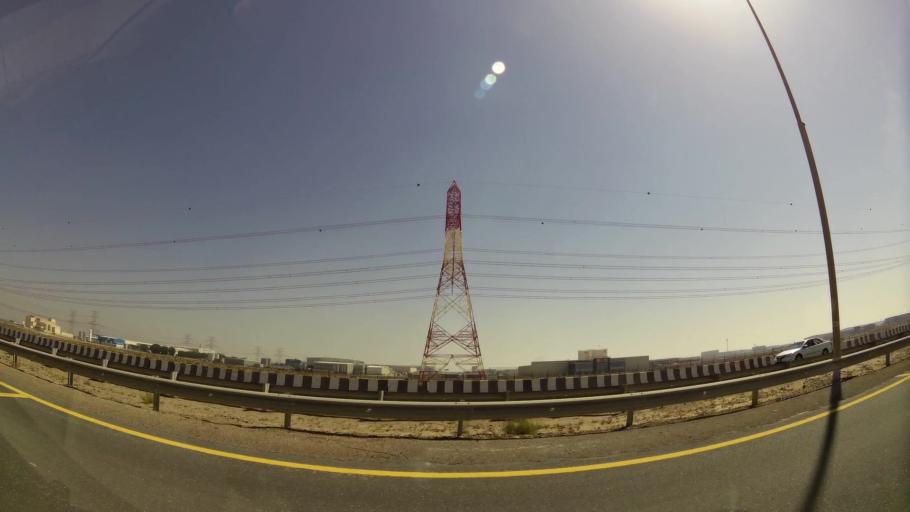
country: AE
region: Dubai
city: Dubai
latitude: 24.9293
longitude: 55.0884
